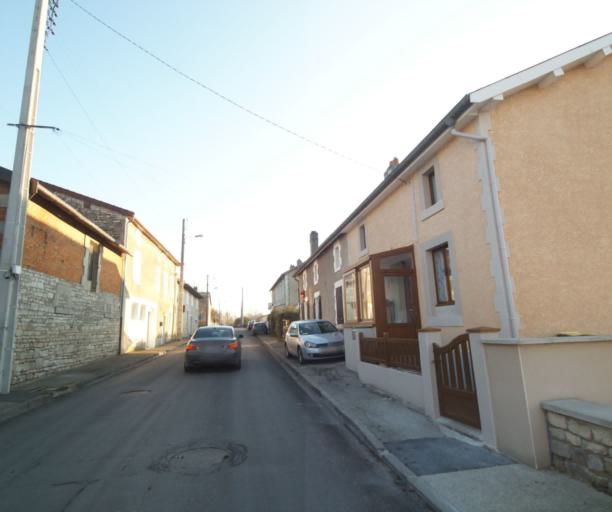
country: FR
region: Champagne-Ardenne
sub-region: Departement de la Haute-Marne
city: Bienville
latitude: 48.5718
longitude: 5.0460
